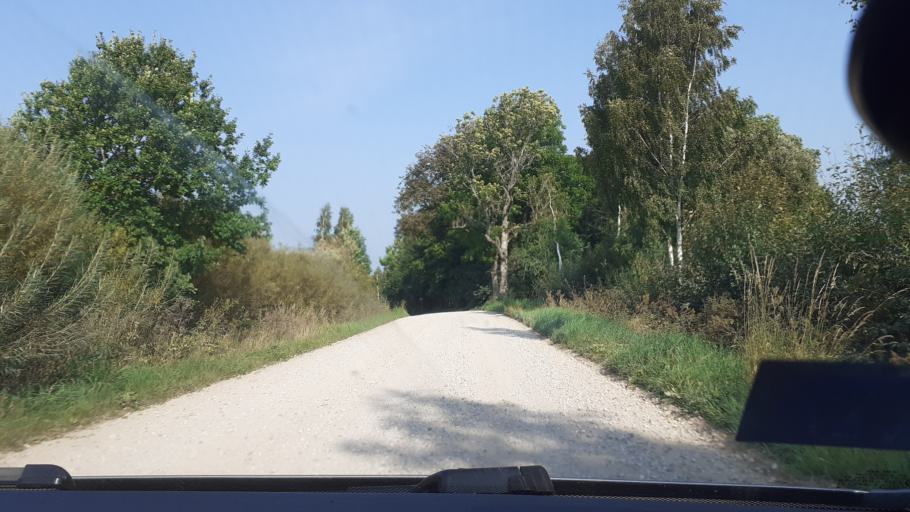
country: LV
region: Kuldigas Rajons
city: Kuldiga
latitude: 56.9849
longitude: 21.8627
